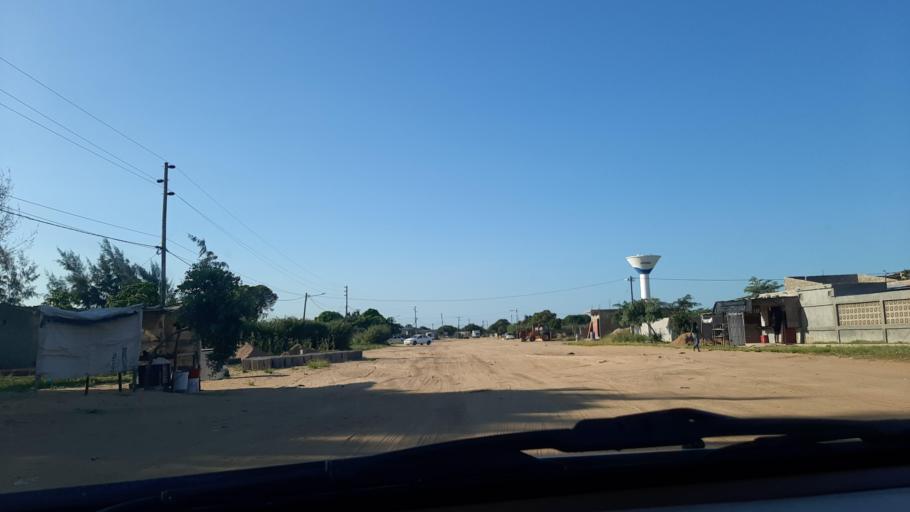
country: MZ
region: Maputo City
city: Maputo
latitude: -25.7904
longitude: 32.5522
